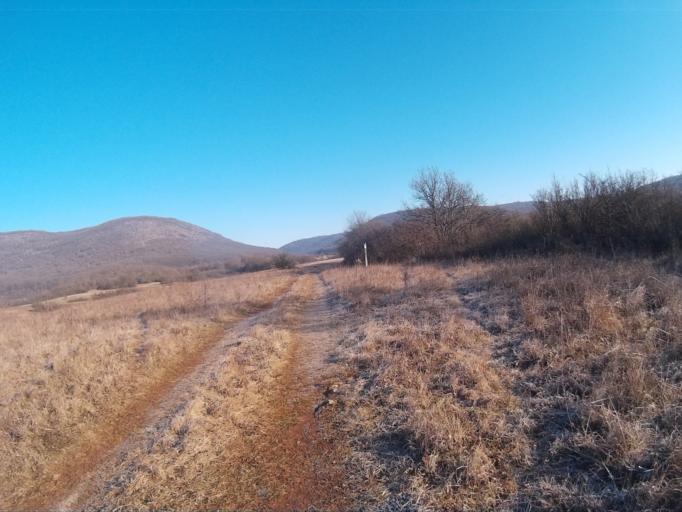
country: HU
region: Borsod-Abauj-Zemplen
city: Rudabanya
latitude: 48.4926
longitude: 20.5564
